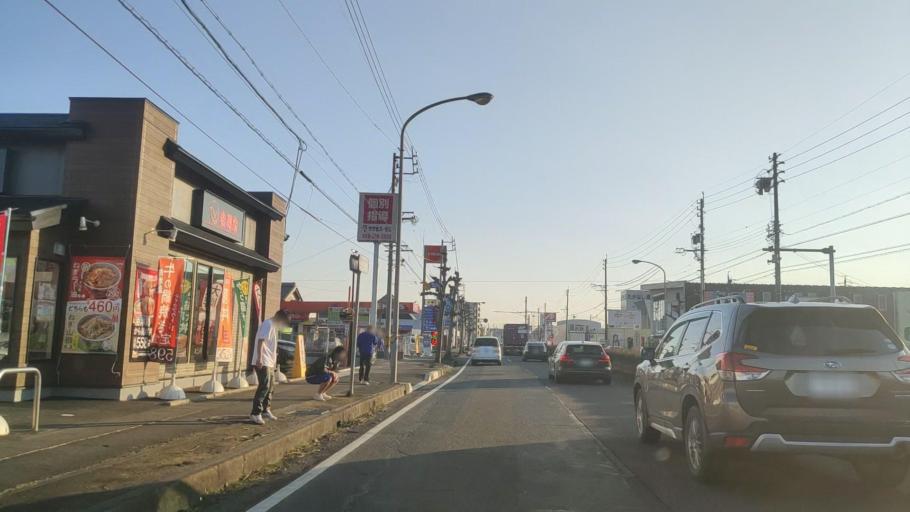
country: JP
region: Gifu
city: Gifu-shi
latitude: 35.4418
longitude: 136.7389
